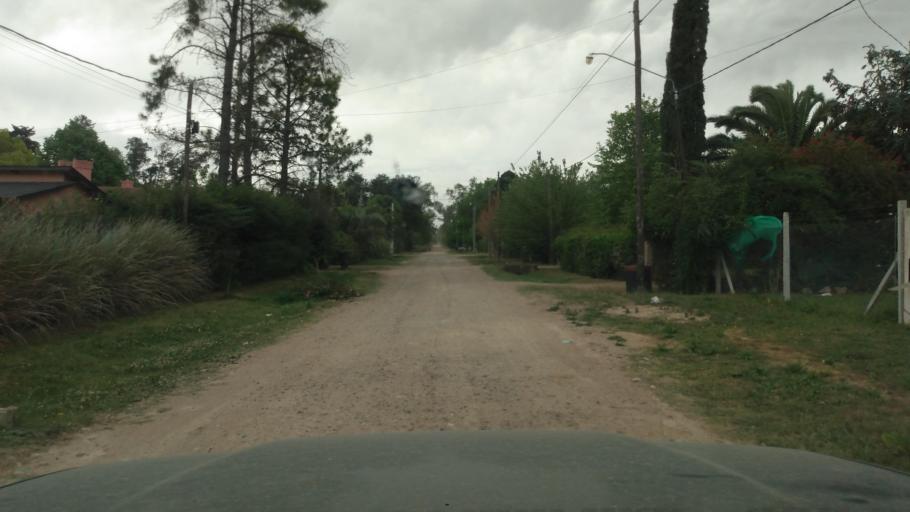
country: AR
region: Buenos Aires
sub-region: Partido de Lujan
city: Lujan
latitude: -34.5936
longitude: -59.1394
